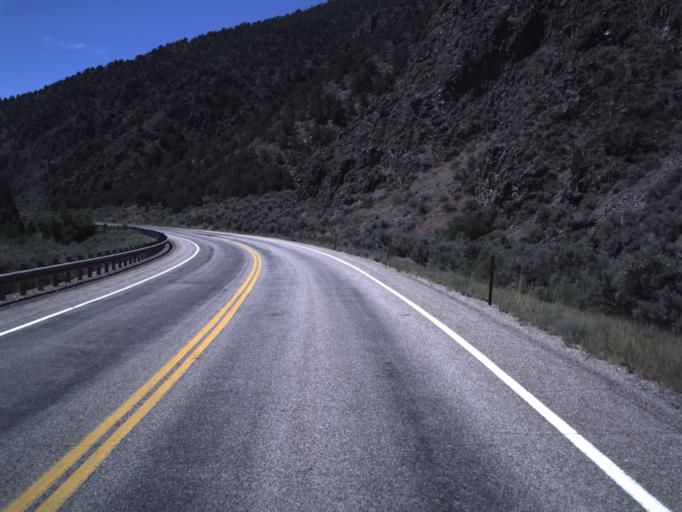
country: US
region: Utah
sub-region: Piute County
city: Junction
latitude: 38.1184
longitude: -112.3378
